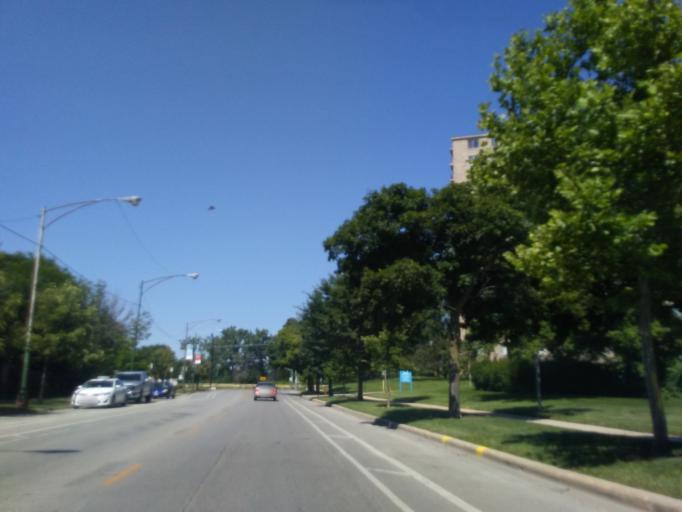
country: US
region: Illinois
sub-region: Cook County
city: Lincolnwood
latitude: 42.0047
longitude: -87.7077
